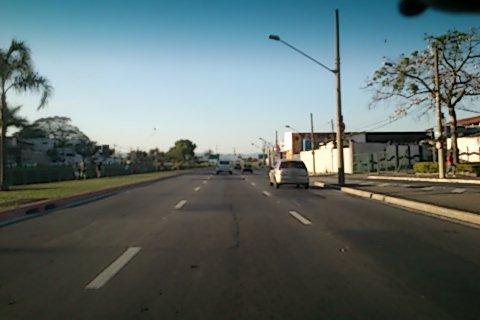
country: BR
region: Sao Paulo
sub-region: Sao Jose Dos Campos
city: Sao Jose dos Campos
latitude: -23.1787
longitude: -45.8760
